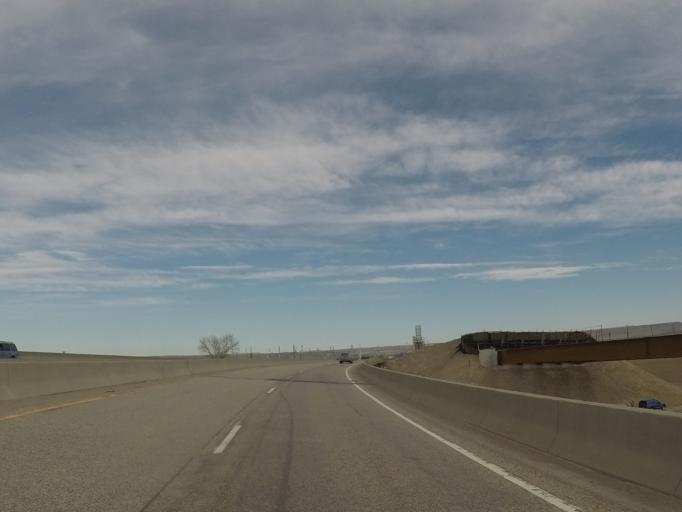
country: US
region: Montana
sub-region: Yellowstone County
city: Laurel
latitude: 45.6642
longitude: -108.7909
